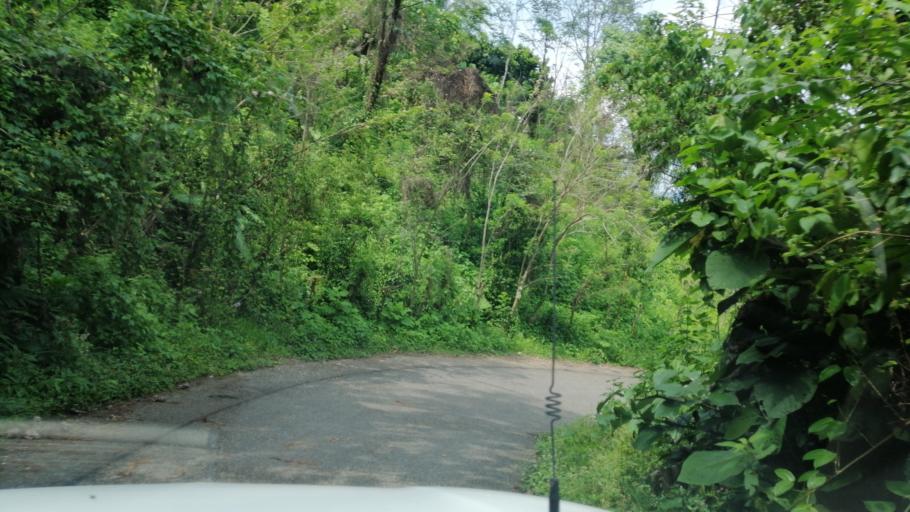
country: MX
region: Chiapas
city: Ostuacan
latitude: 17.3927
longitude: -93.3358
